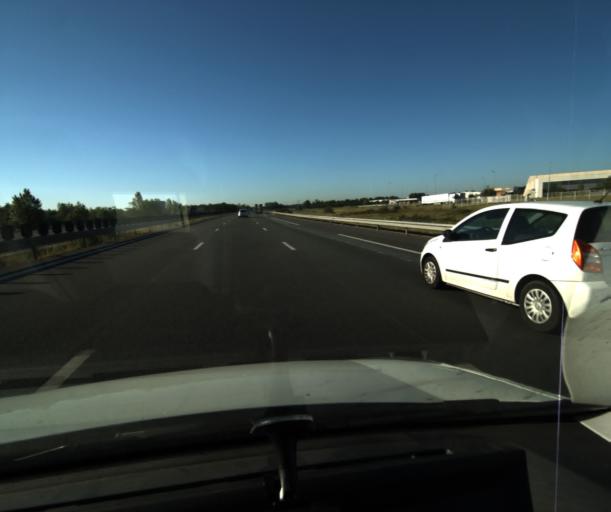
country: FR
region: Midi-Pyrenees
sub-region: Departement du Tarn-et-Garonne
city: Campsas
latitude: 43.9184
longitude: 1.3178
